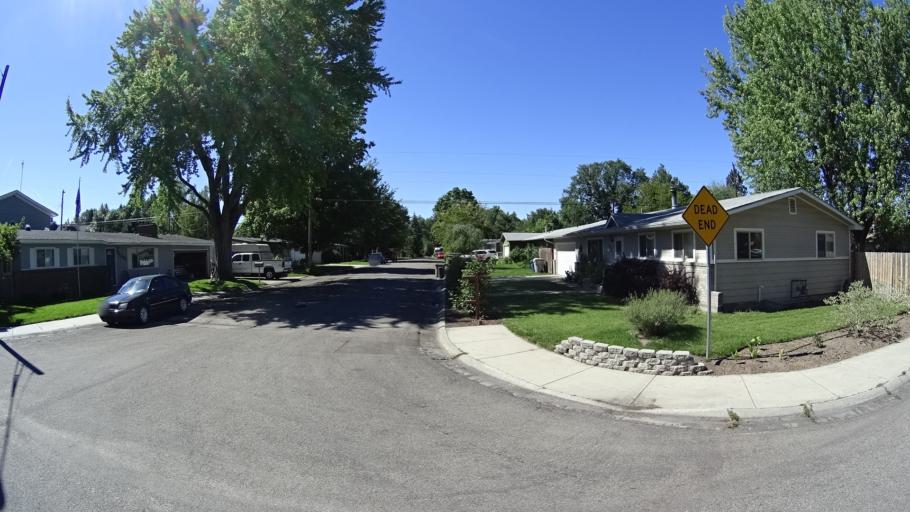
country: US
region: Idaho
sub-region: Ada County
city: Garden City
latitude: 43.6432
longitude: -116.2297
